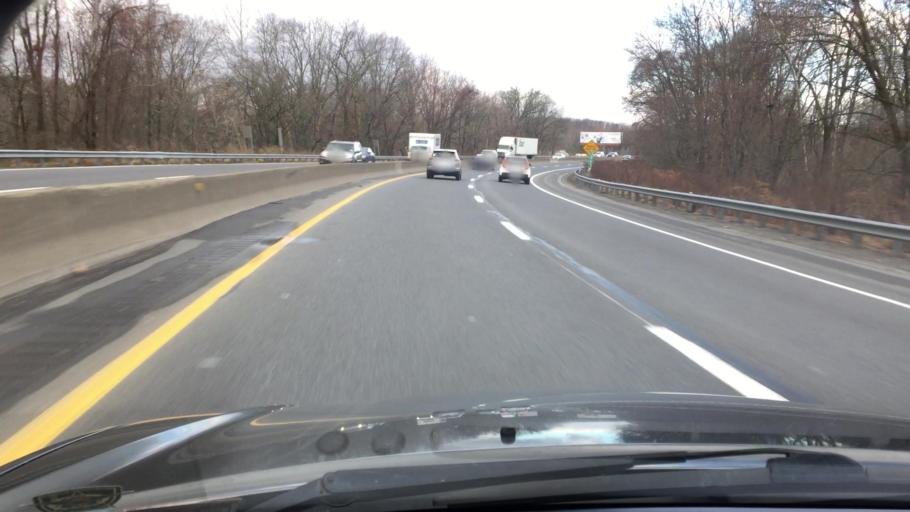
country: US
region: Pennsylvania
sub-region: Monroe County
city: Stroudsburg
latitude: 40.9788
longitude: -75.1976
